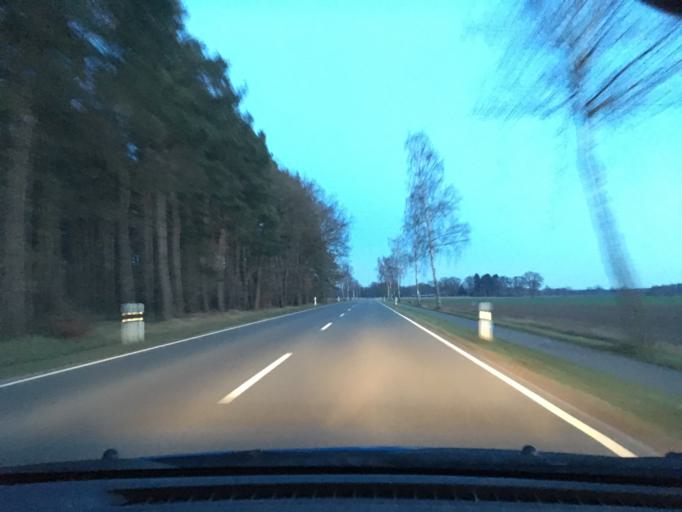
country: DE
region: Lower Saxony
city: Oldendorf
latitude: 53.1856
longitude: 10.2073
